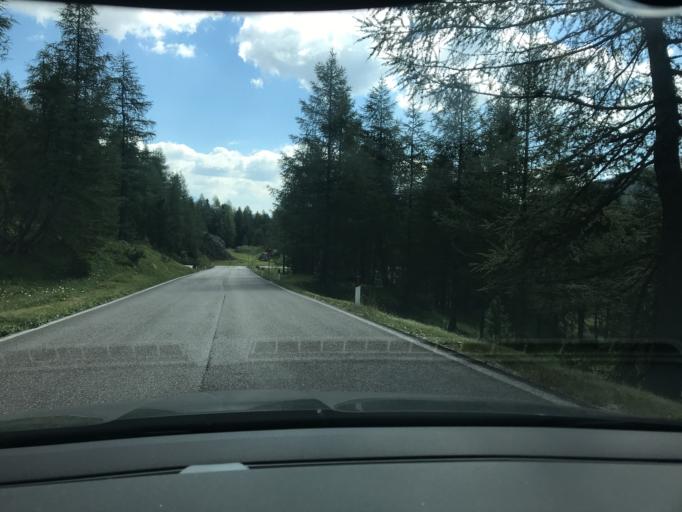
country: IT
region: Veneto
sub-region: Provincia di Belluno
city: Colle Santa Lucia
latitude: 46.5197
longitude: 12.0251
